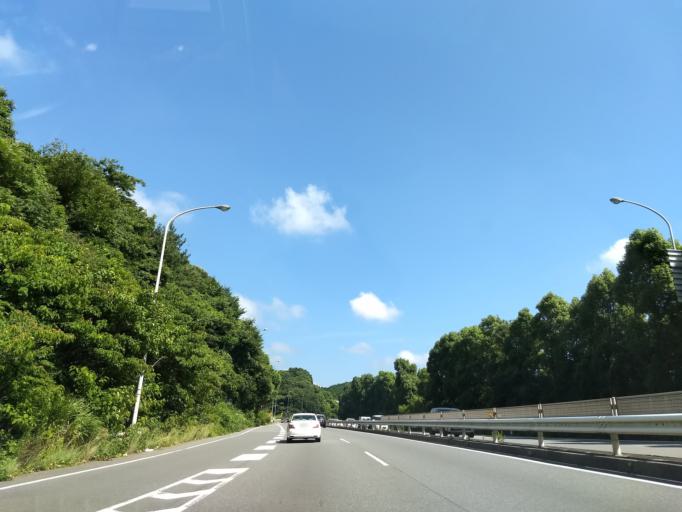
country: JP
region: Shizuoka
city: Mishima
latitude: 35.1726
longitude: 138.9008
